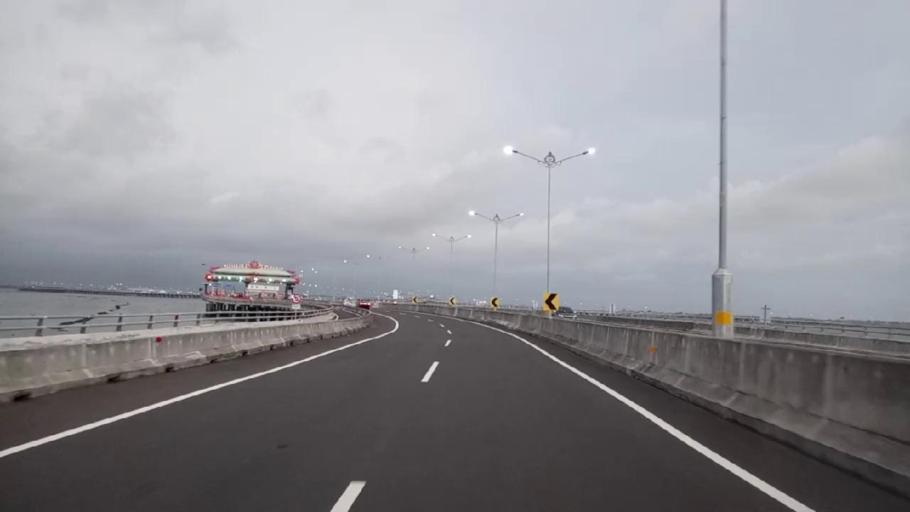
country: ID
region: Bali
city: Kelanabian
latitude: -8.7449
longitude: 115.1857
